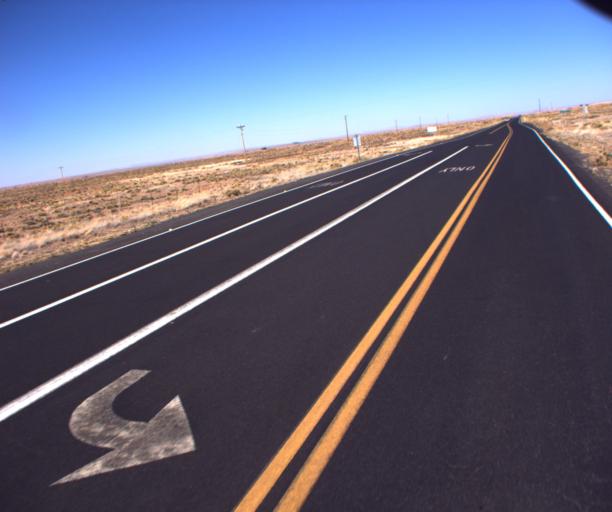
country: US
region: Arizona
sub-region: Navajo County
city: Dilkon
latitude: 35.4947
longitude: -110.4324
